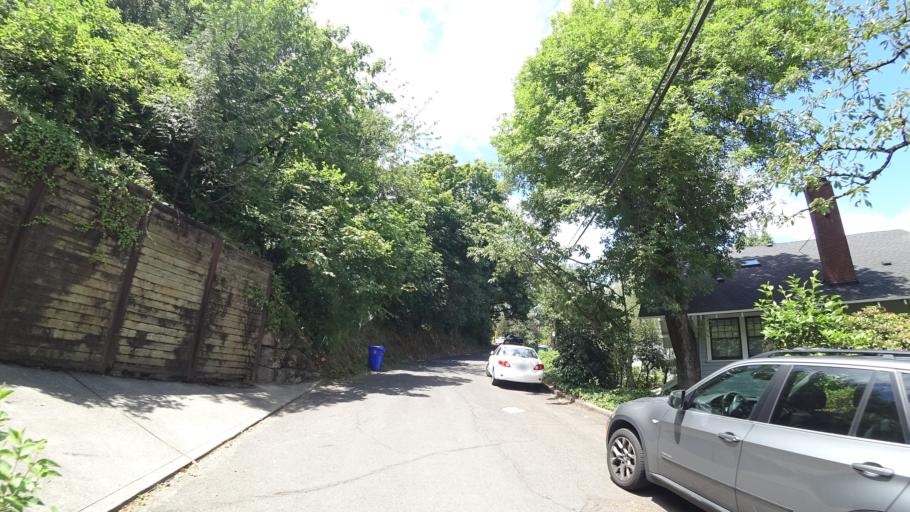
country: US
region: Oregon
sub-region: Multnomah County
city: Portland
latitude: 45.5313
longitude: -122.7076
